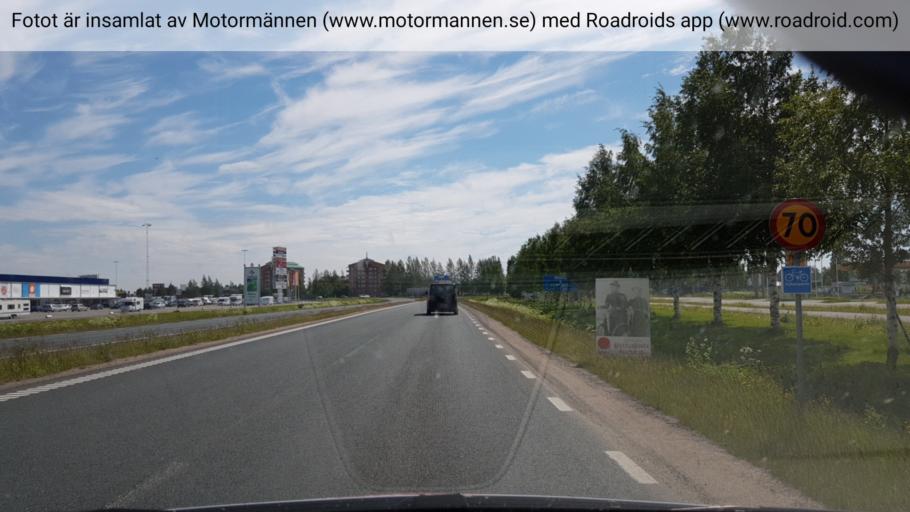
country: SE
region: Norrbotten
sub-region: Haparanda Kommun
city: Haparanda
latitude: 65.8447
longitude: 24.1245
